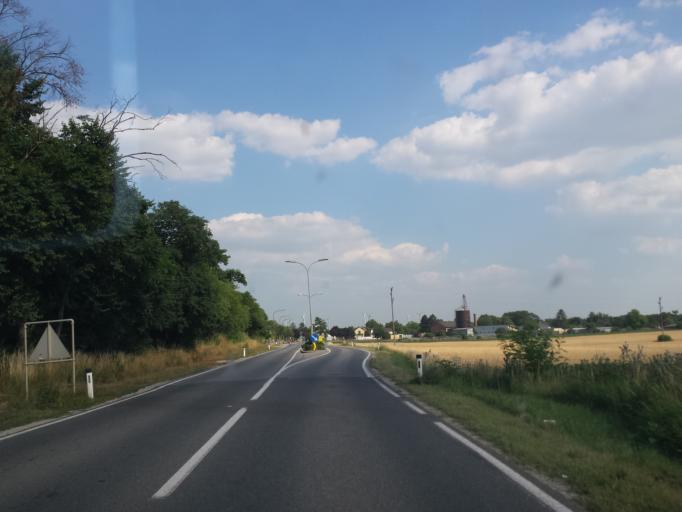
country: AT
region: Lower Austria
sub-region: Politischer Bezirk Ganserndorf
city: Markgrafneusiedl
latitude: 48.2719
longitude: 16.6238
